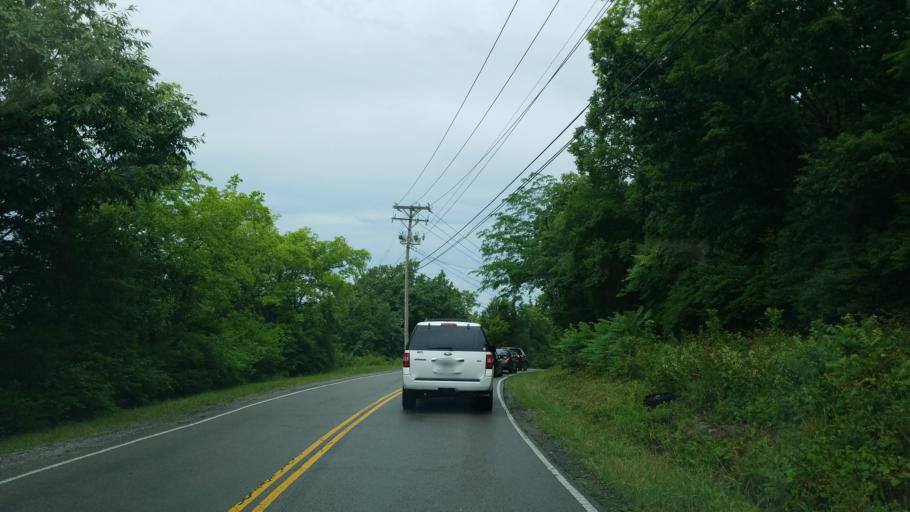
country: US
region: Tennessee
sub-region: Rutherford County
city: La Vergne
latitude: 36.0515
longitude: -86.6668
